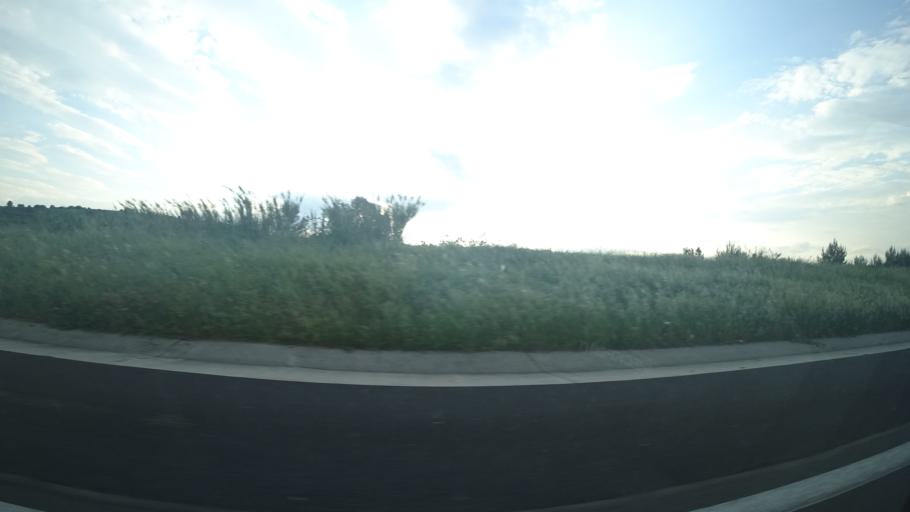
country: FR
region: Languedoc-Roussillon
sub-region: Departement de l'Herault
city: Aspiran
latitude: 43.5624
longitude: 3.4664
